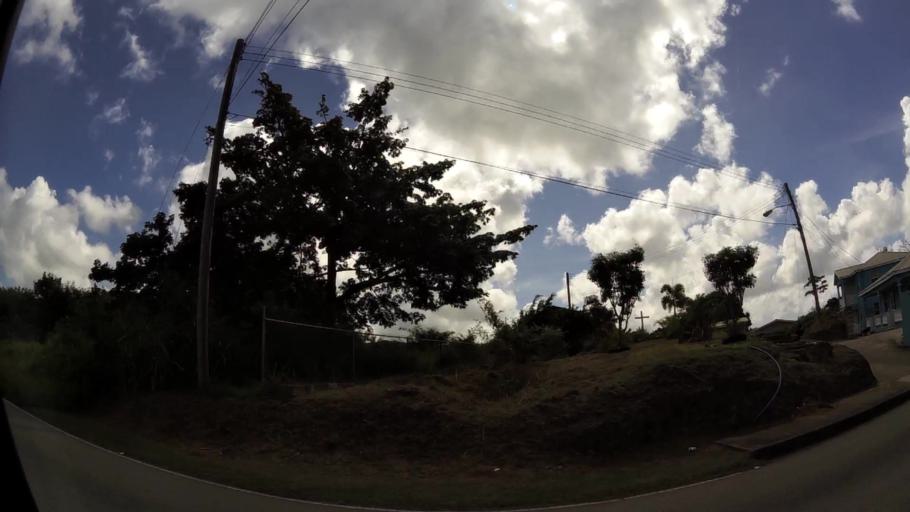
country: BB
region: Saint James
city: Holetown
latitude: 13.1985
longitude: -59.6212
